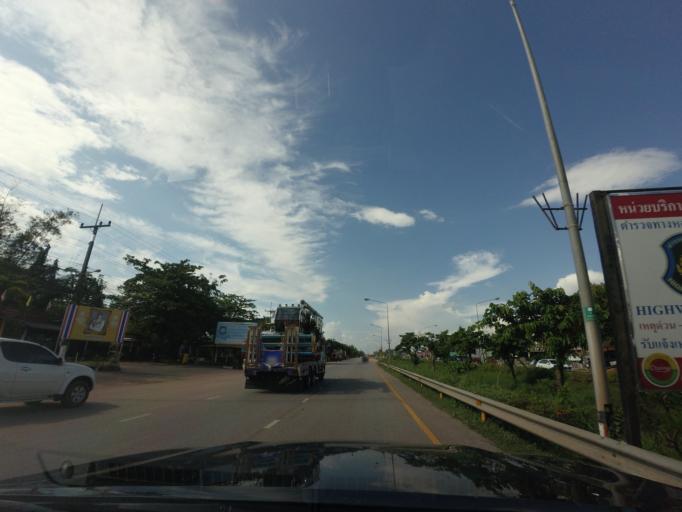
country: TH
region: Nong Khai
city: Sa Khrai
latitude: 17.6882
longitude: 102.7833
